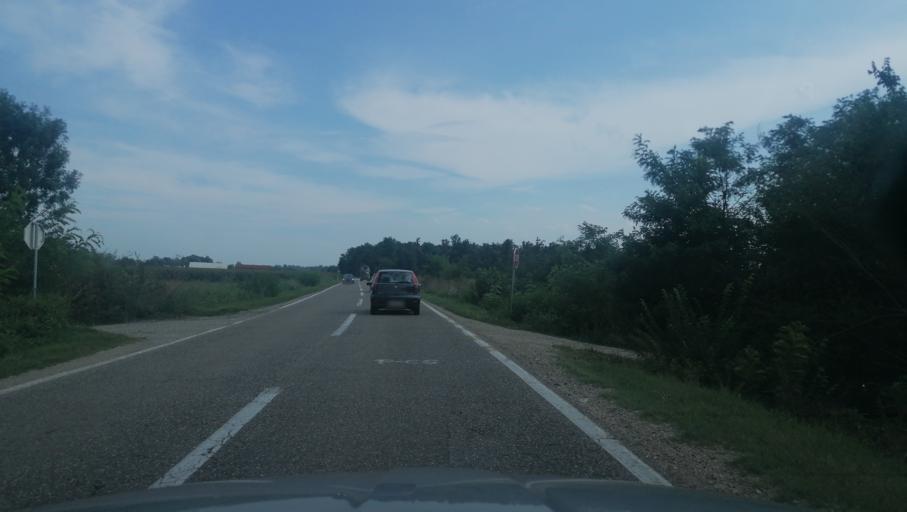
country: HR
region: Vukovarsko-Srijemska
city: Soljani
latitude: 44.8310
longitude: 19.0004
